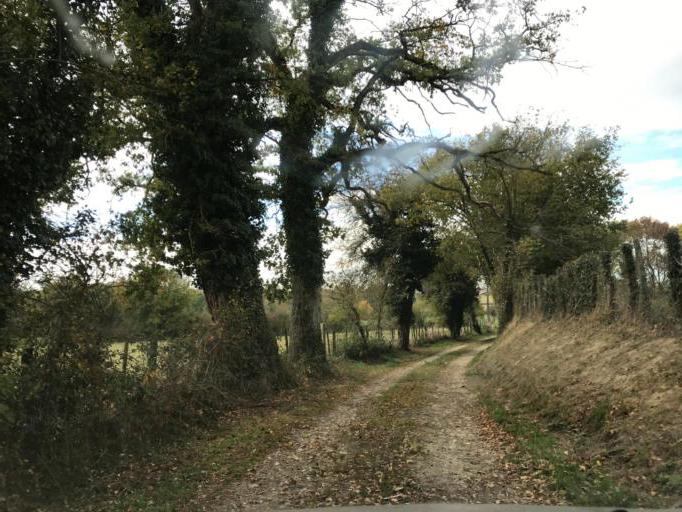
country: FR
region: Rhone-Alpes
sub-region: Departement de l'Ain
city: Beligneux
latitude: 45.9002
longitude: 5.1269
